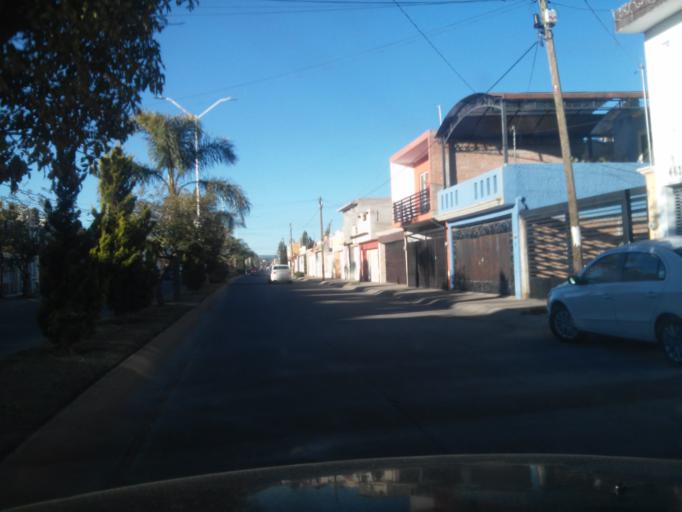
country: MX
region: Durango
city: Victoria de Durango
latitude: 24.0036
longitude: -104.6375
